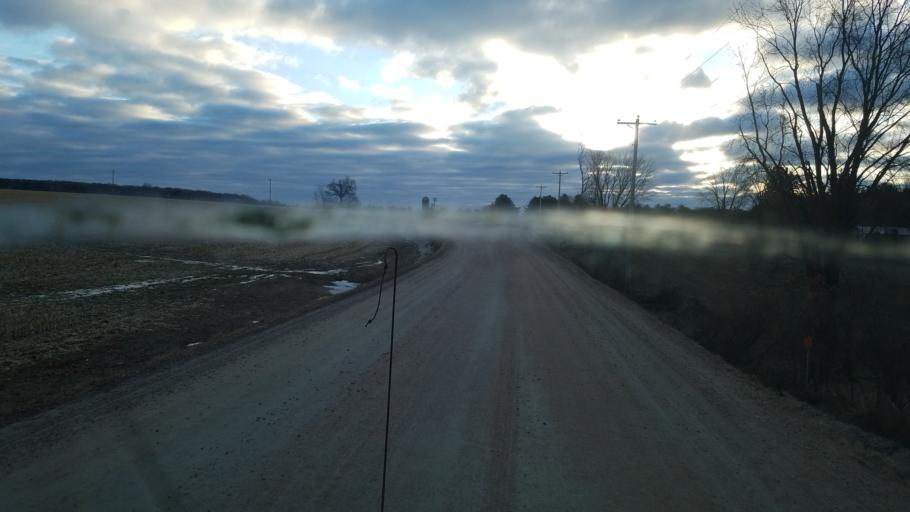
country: US
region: Wisconsin
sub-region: Clark County
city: Neillsville
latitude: 44.5965
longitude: -90.4599
